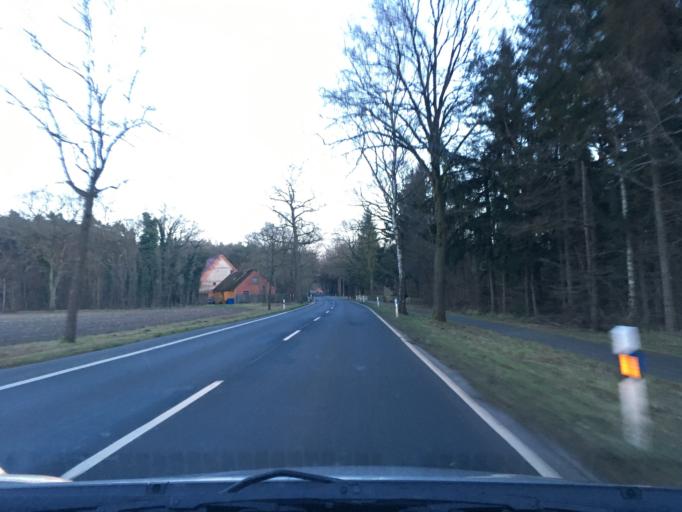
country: DE
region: Lower Saxony
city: Waddeweitz
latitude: 52.9829
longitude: 11.0112
